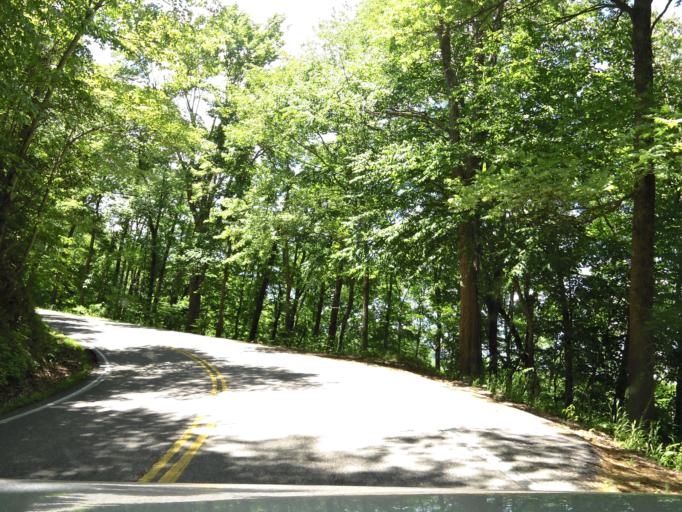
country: US
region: North Carolina
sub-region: Graham County
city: Robbinsville
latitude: 35.4844
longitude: -83.9328
